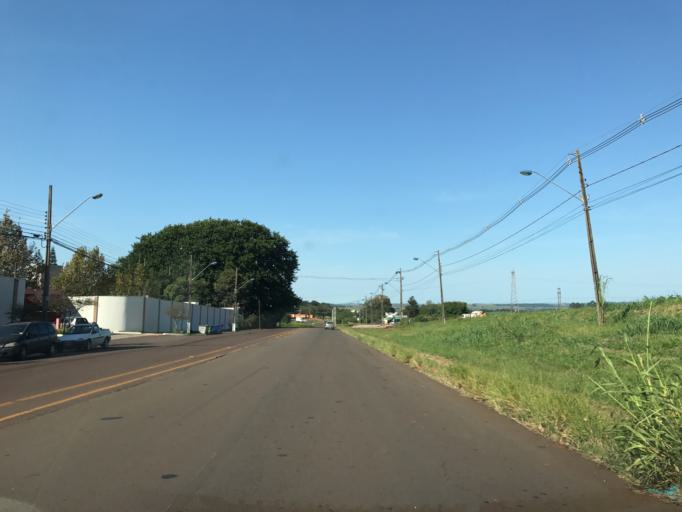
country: BR
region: Parana
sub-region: Maringa
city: Maringa
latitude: -23.4545
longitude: -51.9532
